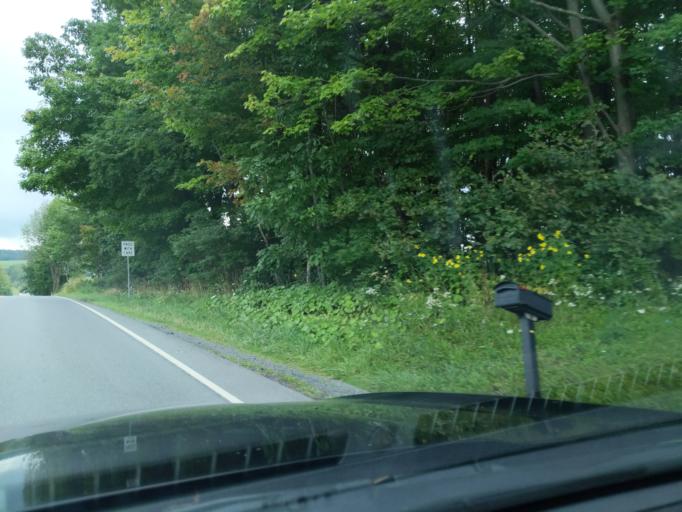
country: US
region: Pennsylvania
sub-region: Cambria County
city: Portage
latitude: 40.3535
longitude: -78.5739
